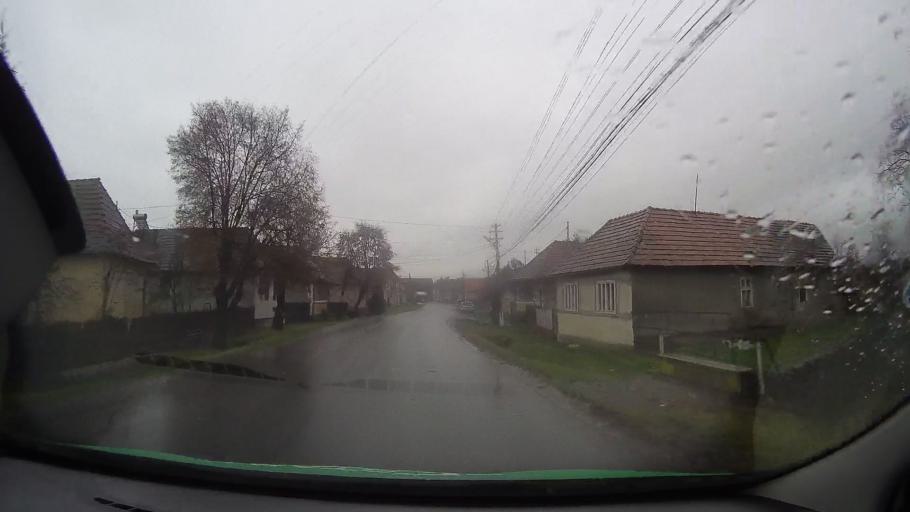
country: RO
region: Mures
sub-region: Comuna Alunis
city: Alunis
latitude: 46.8963
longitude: 24.8224
